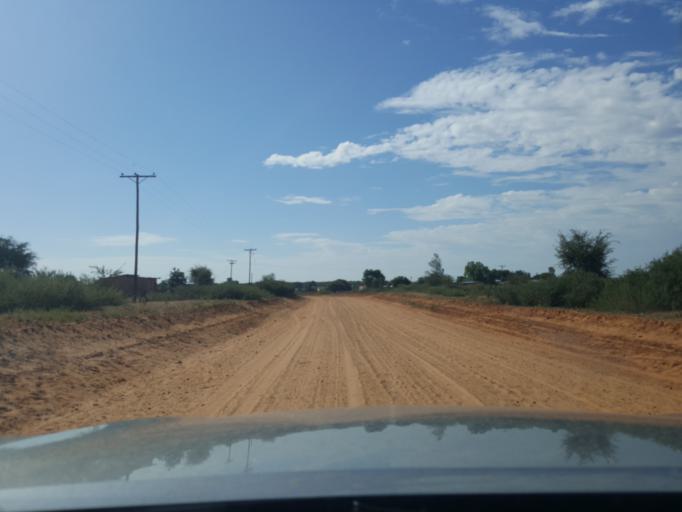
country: BW
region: Kweneng
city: Khudumelapye
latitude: -23.6999
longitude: 24.7205
